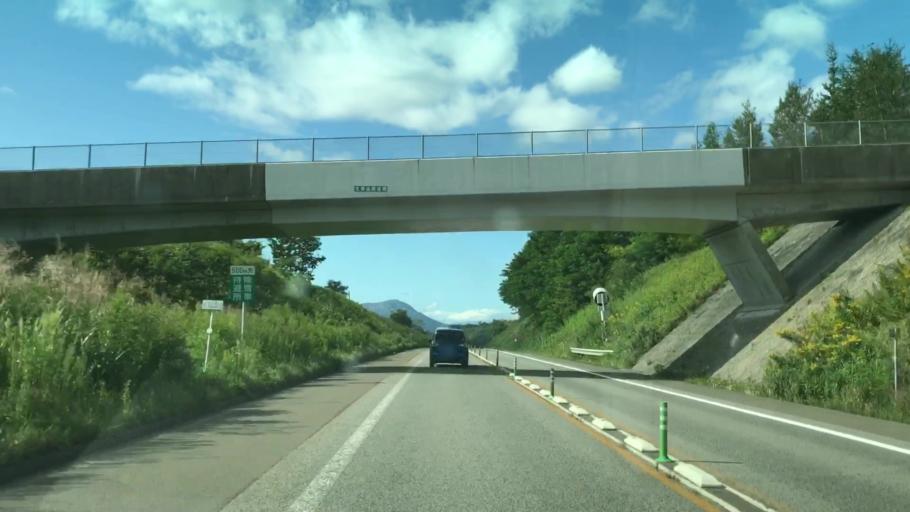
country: JP
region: Hokkaido
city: Date
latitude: 42.4241
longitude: 140.9289
